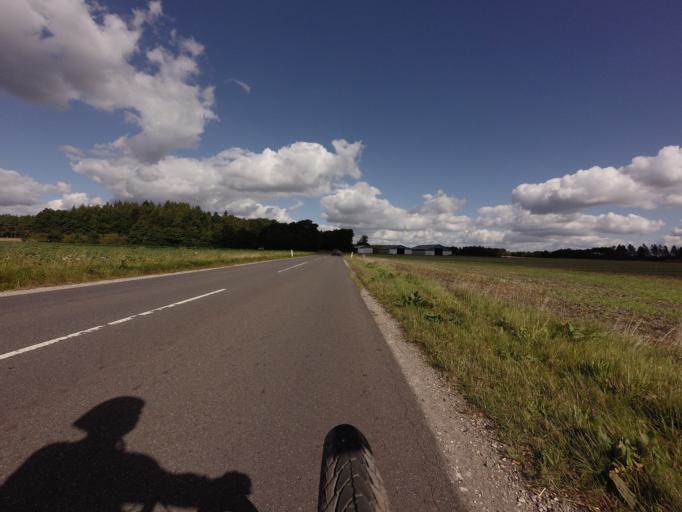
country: DK
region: Central Jutland
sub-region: Ikast-Brande Kommune
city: Brande
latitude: 55.9792
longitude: 9.1437
